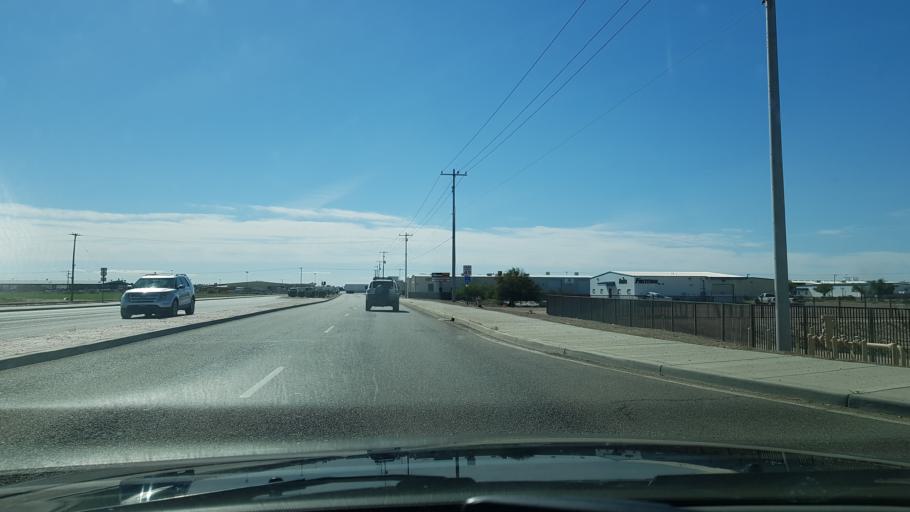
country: US
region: Arizona
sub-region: Yuma County
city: Yuma
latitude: 32.6798
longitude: -114.5818
